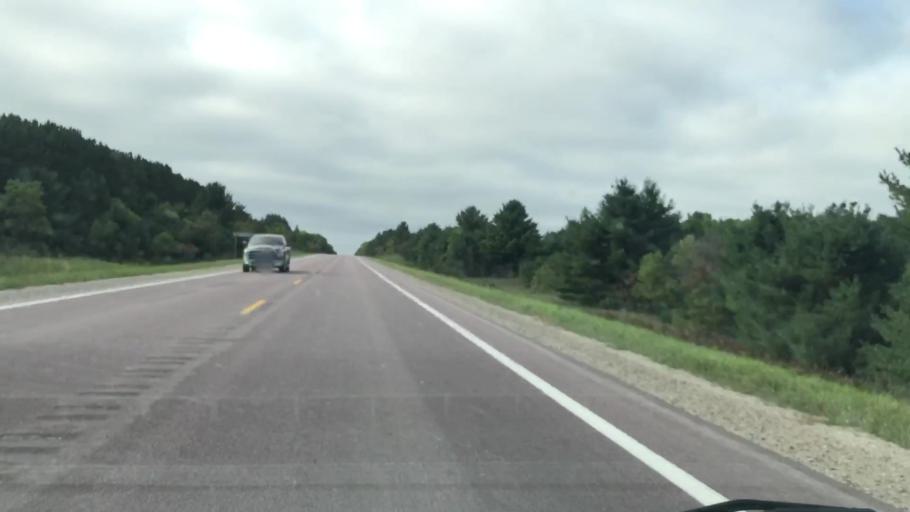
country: US
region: Michigan
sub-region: Luce County
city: Newberry
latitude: 46.2877
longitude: -85.5702
